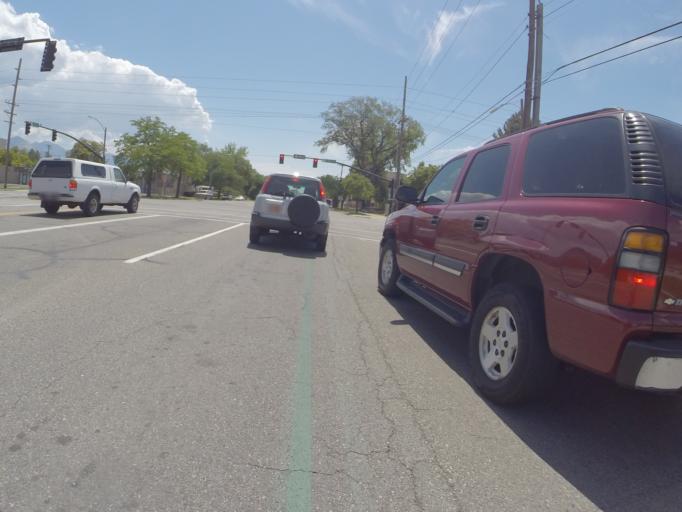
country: US
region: Utah
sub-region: Salt Lake County
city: Salt Lake City
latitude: 40.7566
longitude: -111.8855
